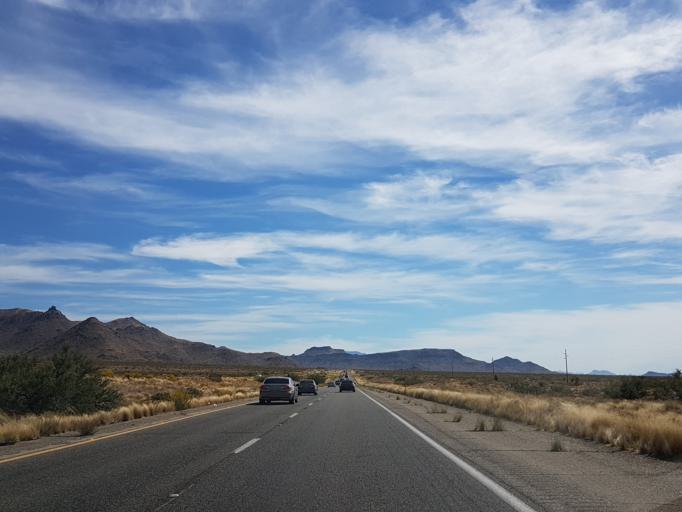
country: US
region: Arizona
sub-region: Mohave County
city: Golden Valley
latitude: 35.2678
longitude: -114.1662
